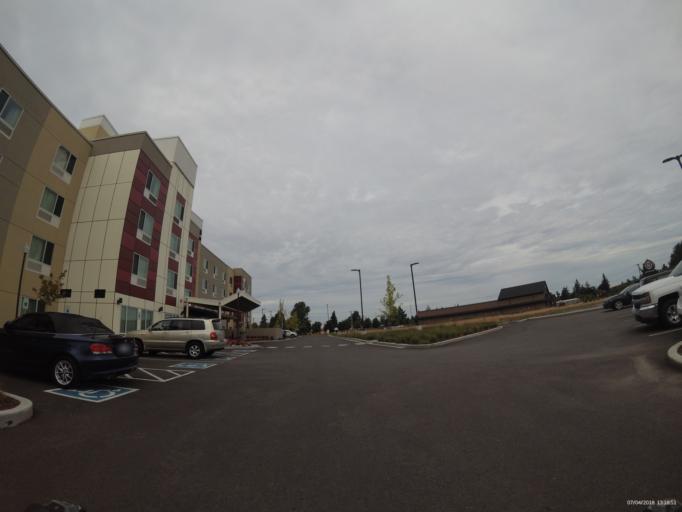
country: US
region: Washington
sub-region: Pierce County
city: McChord Air Force Base
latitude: 47.1498
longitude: -122.5011
